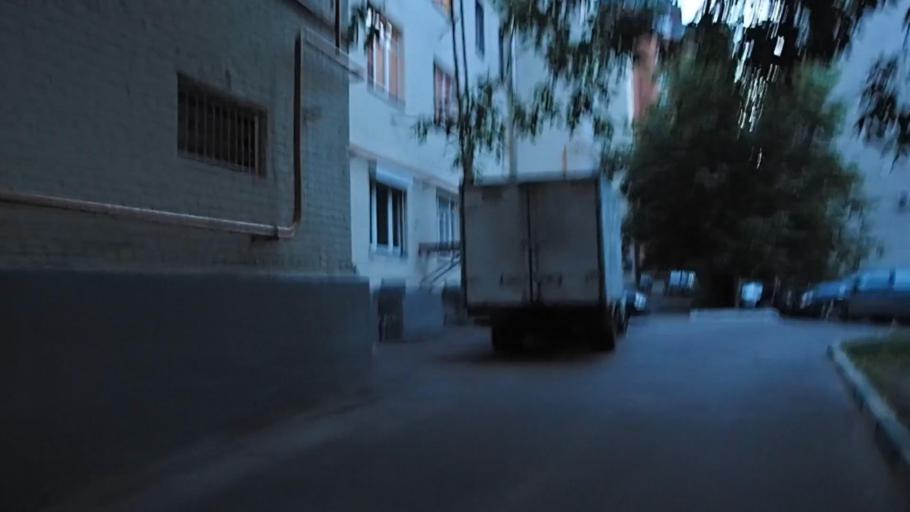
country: RU
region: Moscow
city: Sokol'niki
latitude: 55.7944
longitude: 37.6924
